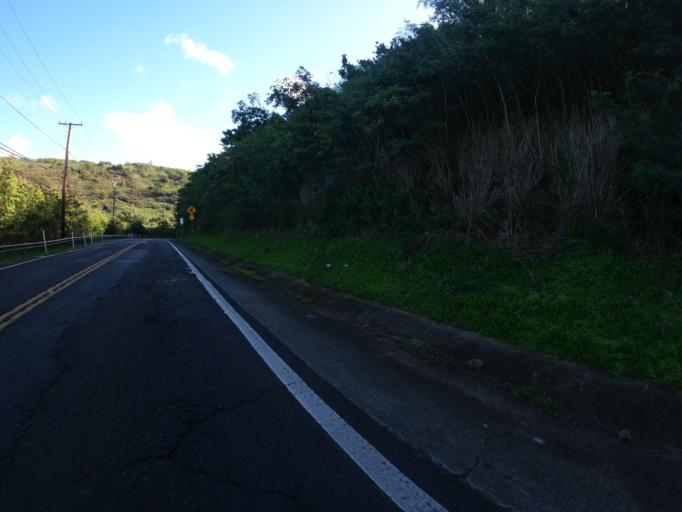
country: US
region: Hawaii
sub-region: Honolulu County
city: Pupukea
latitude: 21.6382
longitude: -158.0627
